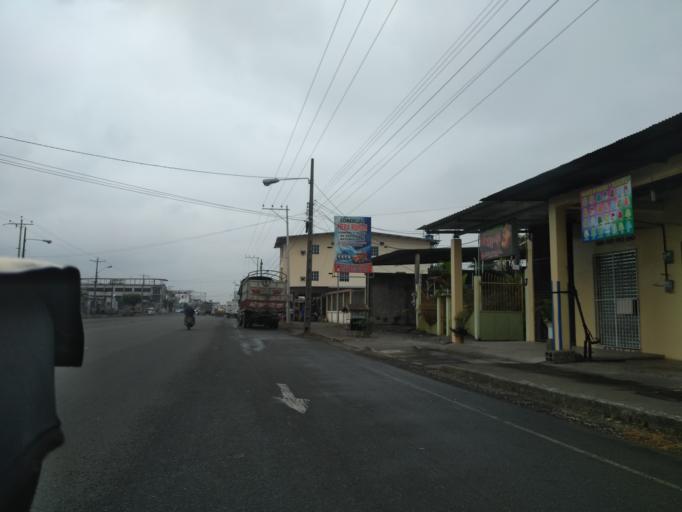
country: EC
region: Cotopaxi
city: La Mana
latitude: -0.9503
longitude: -79.3462
